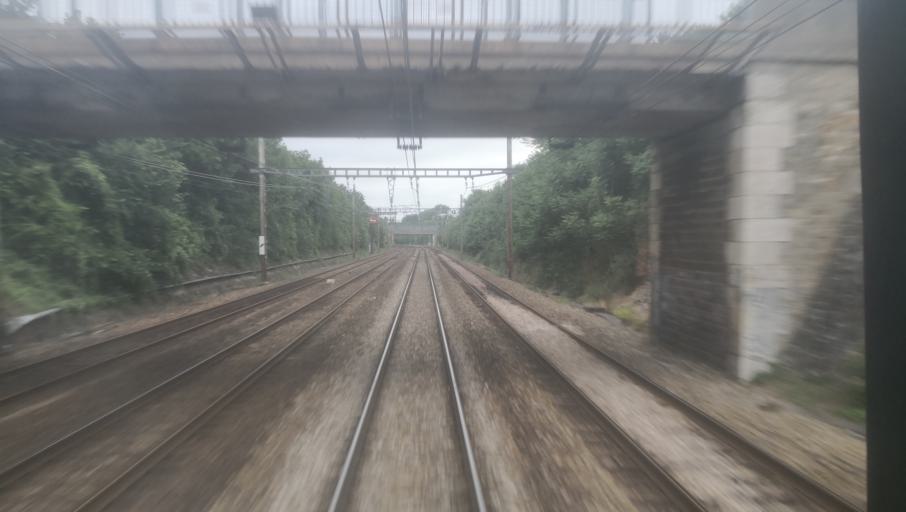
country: FR
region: Ile-de-France
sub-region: Departement de l'Essonne
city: Bretigny-sur-Orge
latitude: 48.6149
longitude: 2.3064
